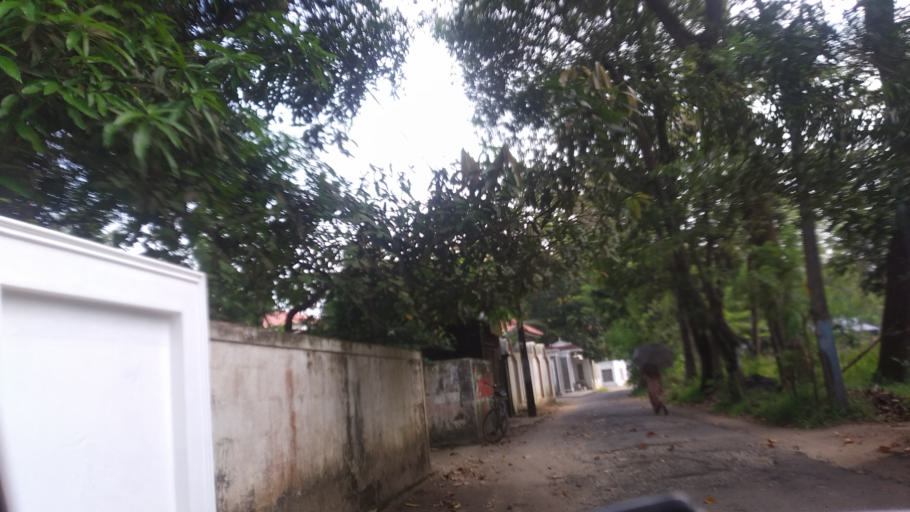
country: IN
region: Kerala
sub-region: Ernakulam
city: Elur
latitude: 10.0880
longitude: 76.2100
